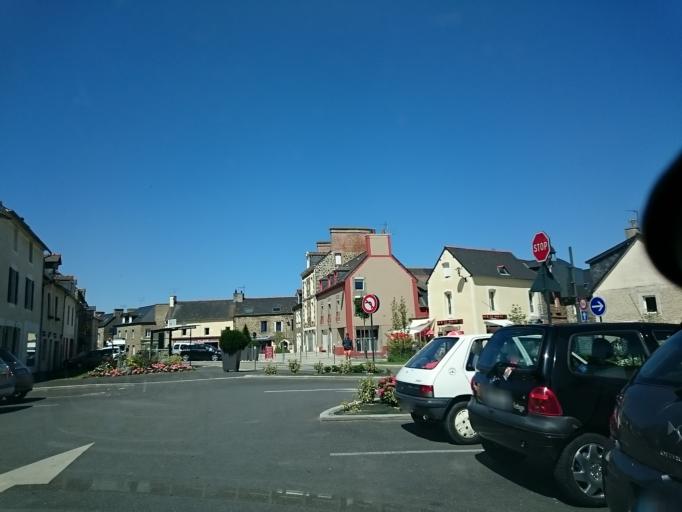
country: FR
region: Brittany
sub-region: Departement d'Ille-et-Vilaine
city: Saint-Meloir-des-Ondes
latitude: 48.6370
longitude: -1.9034
